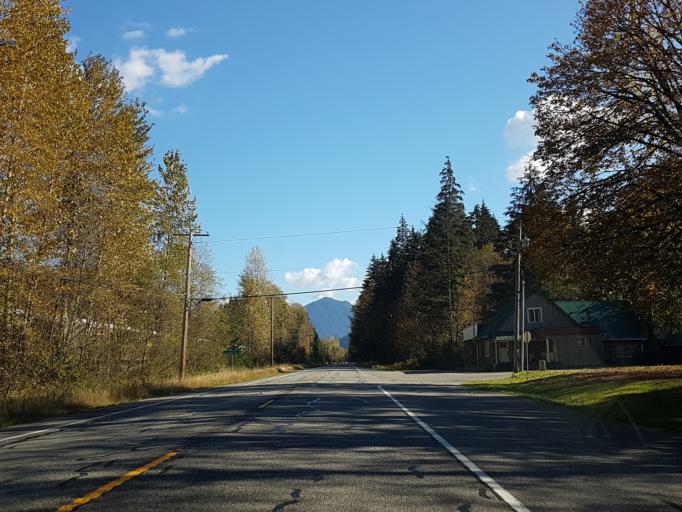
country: US
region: Washington
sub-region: Snohomish County
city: Gold Bar
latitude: 47.7667
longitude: -121.4782
